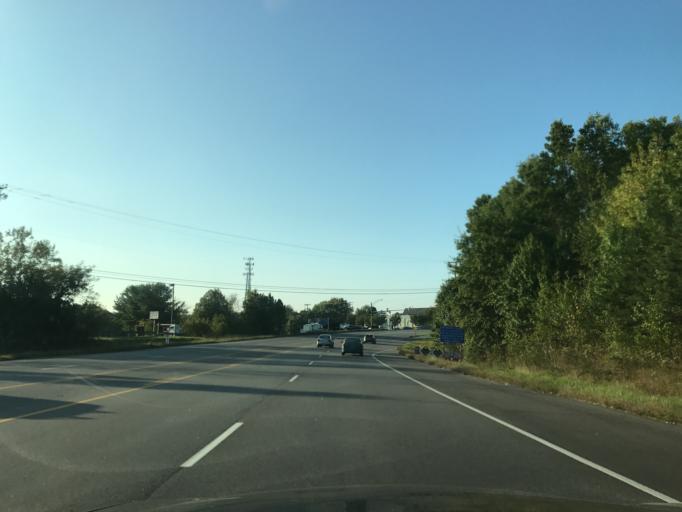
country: US
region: Maryland
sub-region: Anne Arundel County
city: South Gate
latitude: 39.0975
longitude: -76.6252
